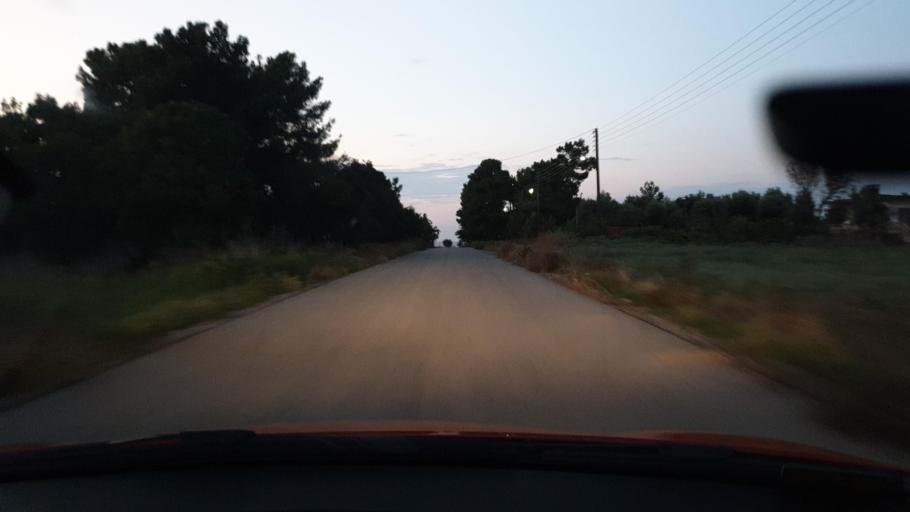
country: GR
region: Central Macedonia
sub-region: Nomos Thessalonikis
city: Agia Triada
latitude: 40.5042
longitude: 22.8326
